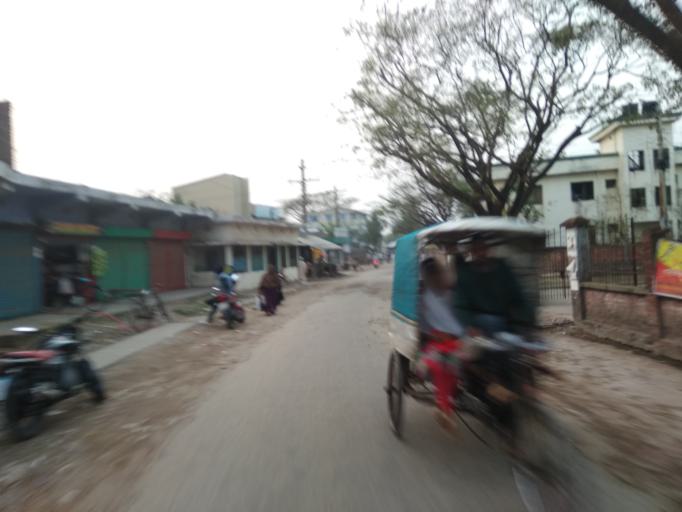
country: IN
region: West Bengal
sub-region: North 24 Parganas
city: Taki
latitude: 22.4554
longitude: 89.0315
